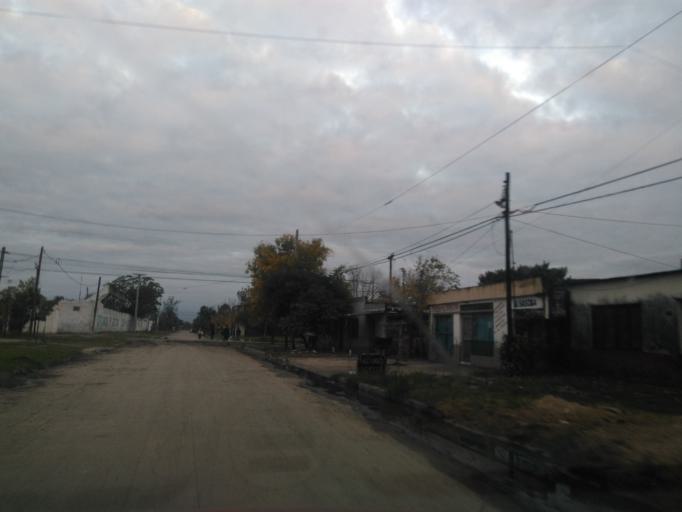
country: AR
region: Chaco
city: Resistencia
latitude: -27.4756
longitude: -58.9961
